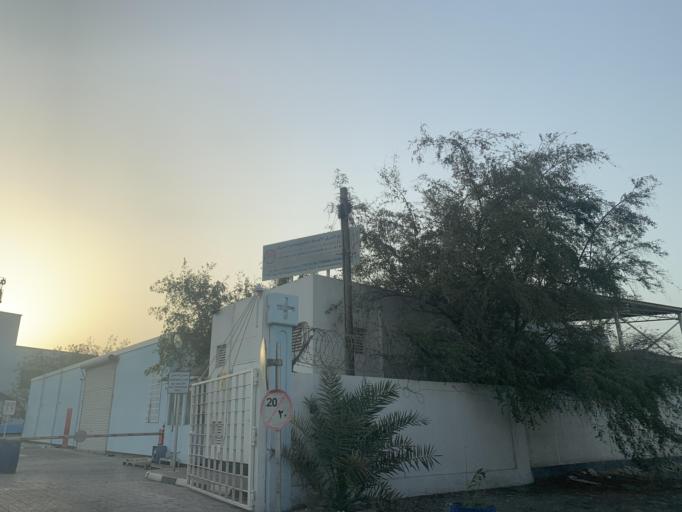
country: BH
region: Manama
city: Manama
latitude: 26.1953
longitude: 50.5940
